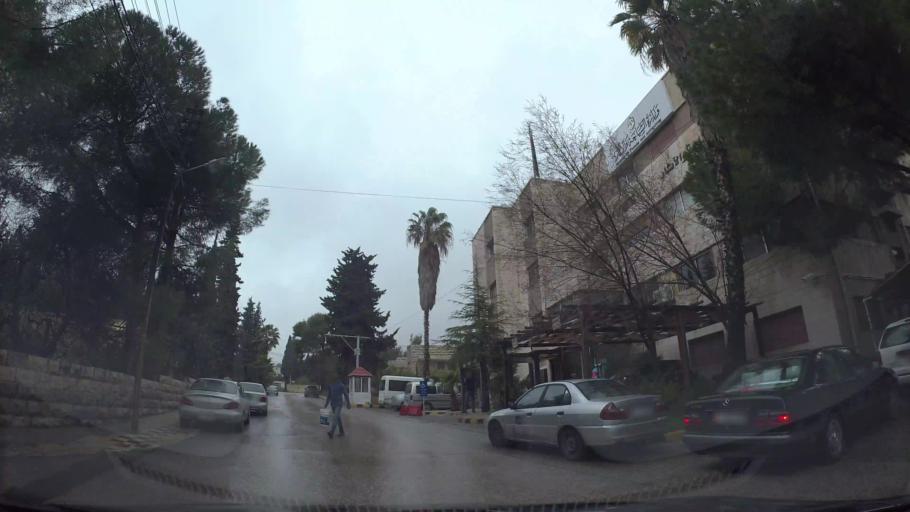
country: JO
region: Amman
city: Amman
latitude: 31.9529
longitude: 35.9077
